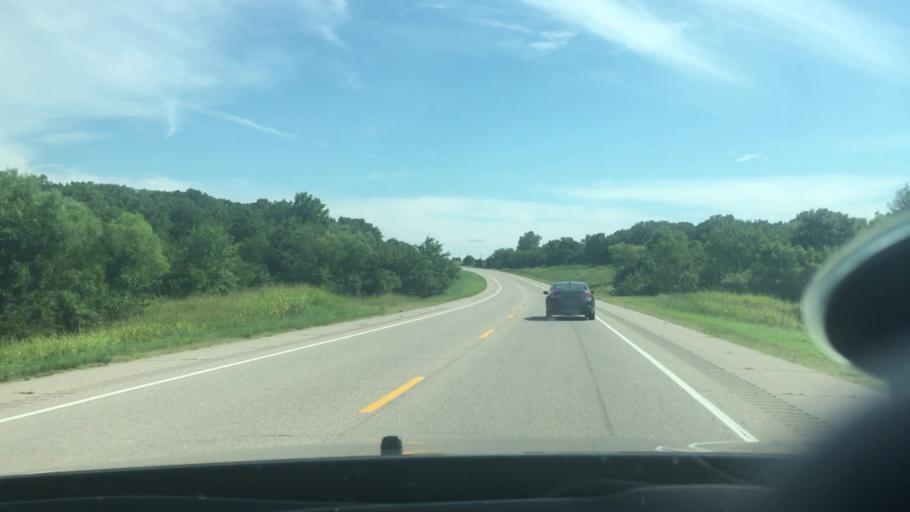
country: US
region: Oklahoma
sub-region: Seminole County
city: Konawa
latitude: 35.0514
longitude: -96.6808
